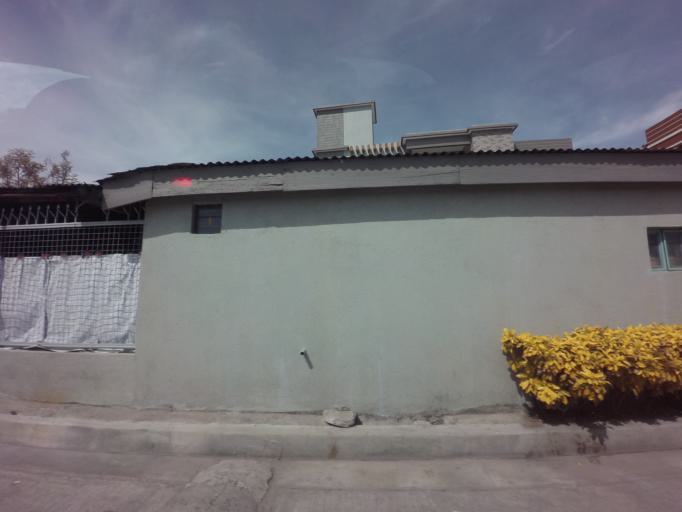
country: PH
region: Calabarzon
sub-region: Province of Rizal
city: Taguig
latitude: 14.5359
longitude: 121.1002
